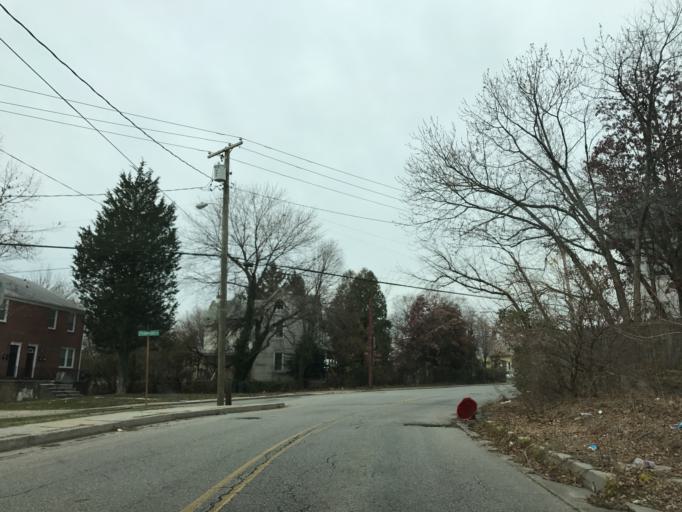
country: US
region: Maryland
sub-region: Baltimore County
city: Parkville
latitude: 39.3477
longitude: -76.5571
